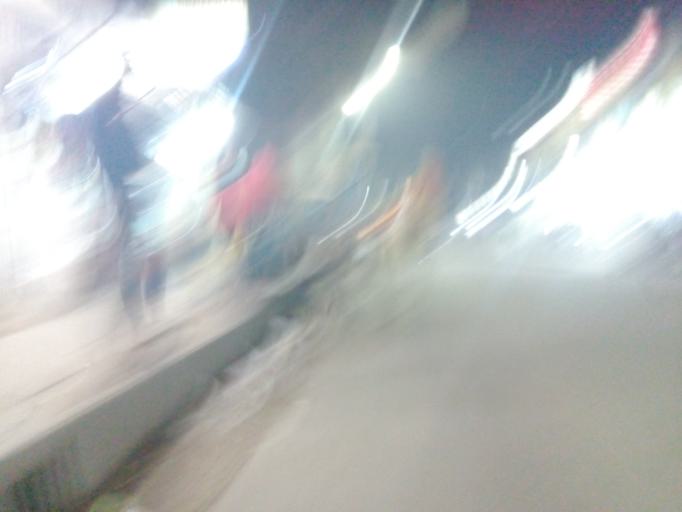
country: BD
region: Dhaka
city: Paltan
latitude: 23.7468
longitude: 90.4283
